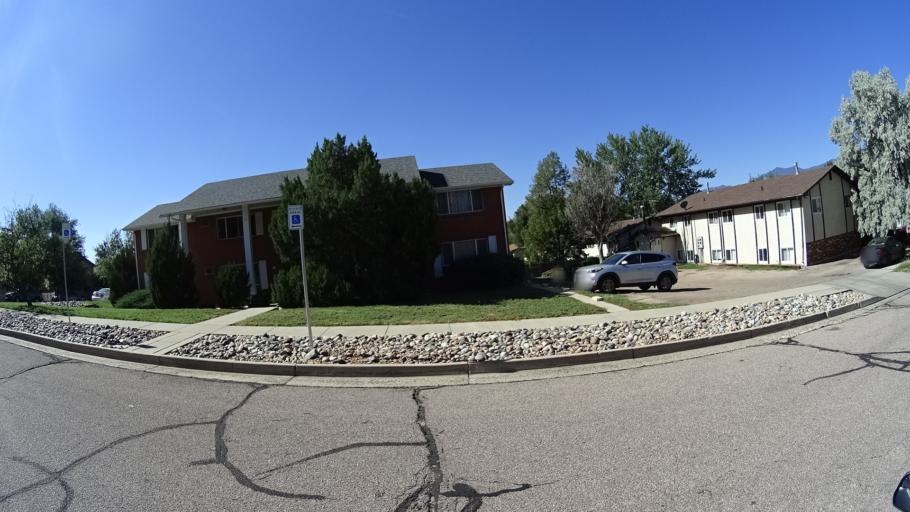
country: US
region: Colorado
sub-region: El Paso County
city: Colorado Springs
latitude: 38.8584
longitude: -104.7874
